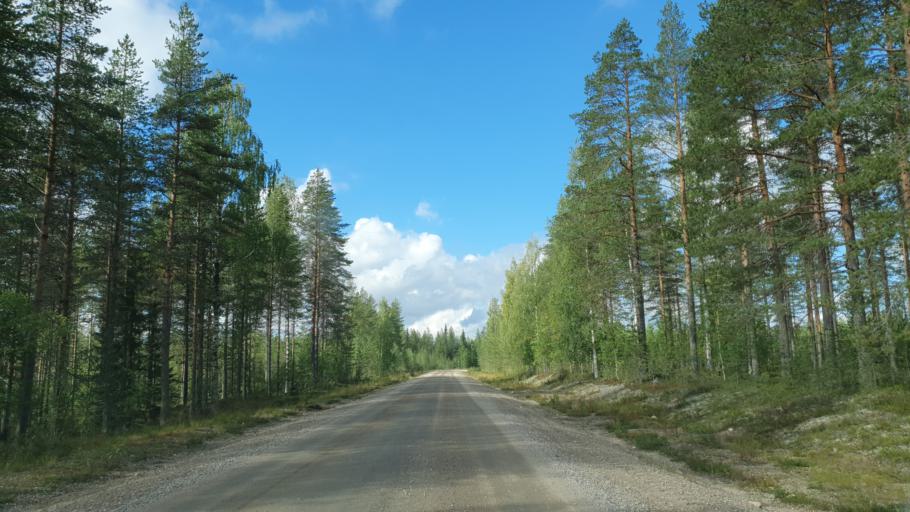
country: FI
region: Kainuu
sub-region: Kehys-Kainuu
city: Kuhmo
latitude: 63.9839
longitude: 29.2373
